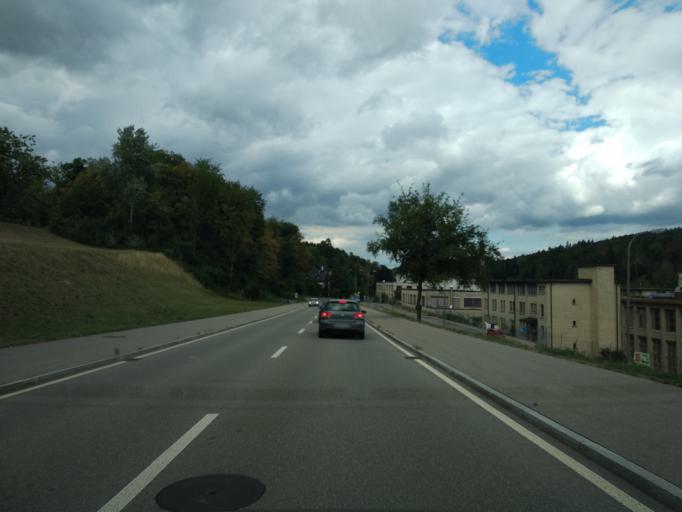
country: CH
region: Zurich
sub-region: Bezirk Pfaeffikon
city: Effretikon / Watt
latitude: 47.4489
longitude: 8.7025
